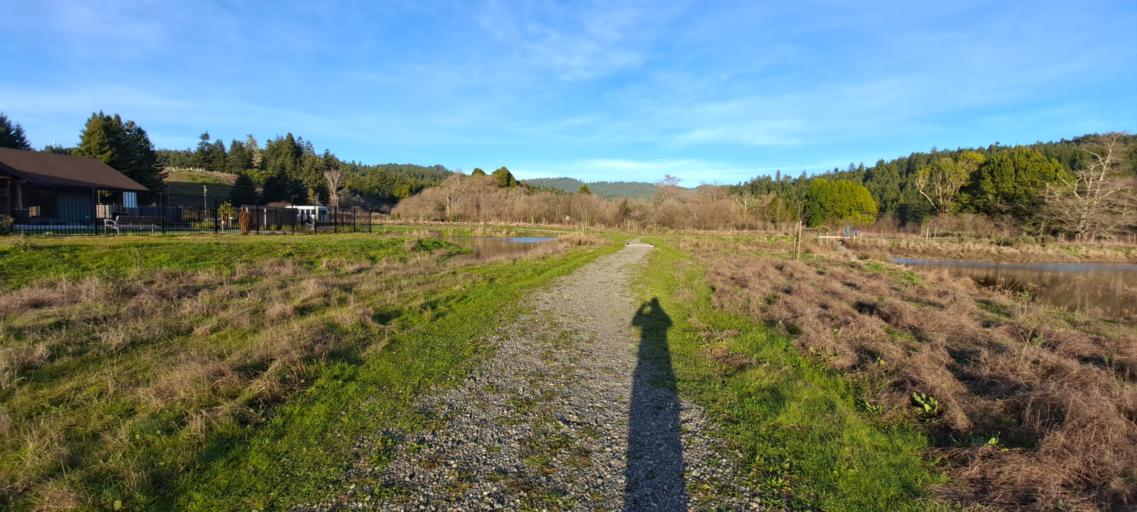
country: US
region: California
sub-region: Humboldt County
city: Fortuna
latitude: 40.5940
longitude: -124.1321
